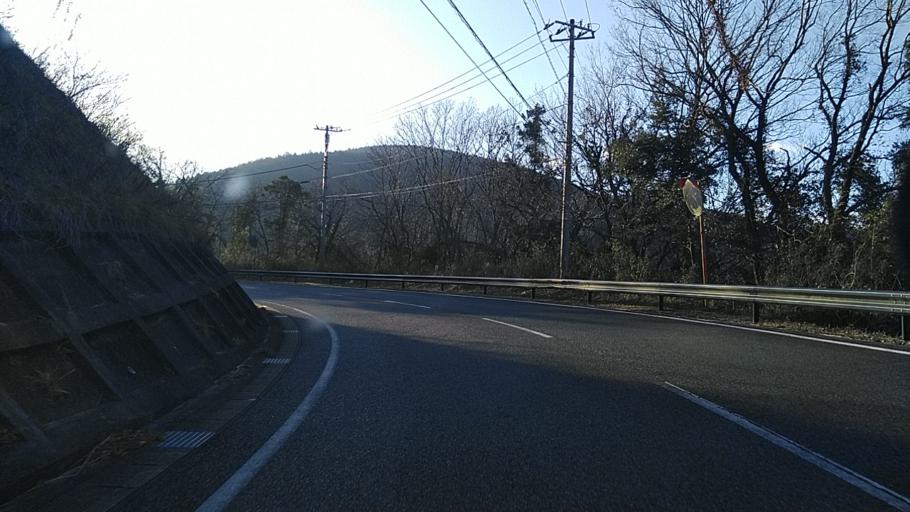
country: JP
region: Chiba
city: Kimitsu
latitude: 35.2588
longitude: 139.9341
